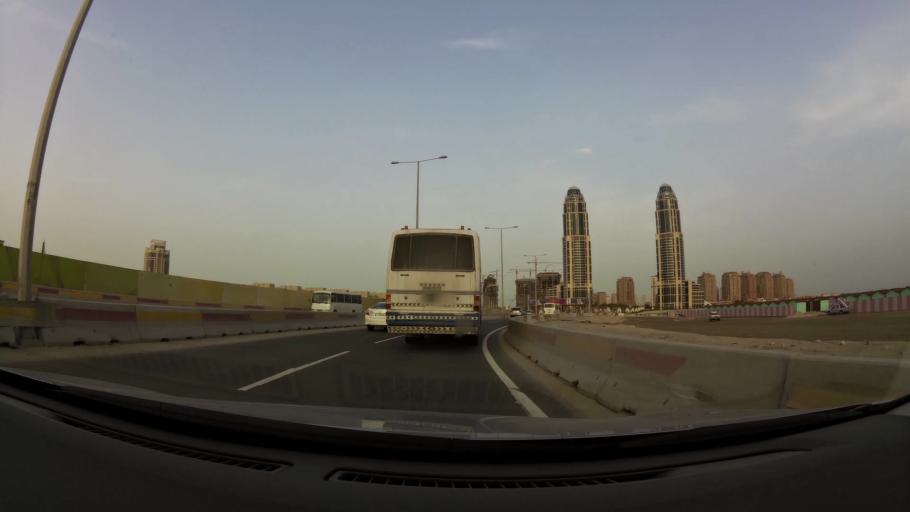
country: QA
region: Baladiyat ad Dawhah
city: Doha
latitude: 25.3731
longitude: 51.5262
